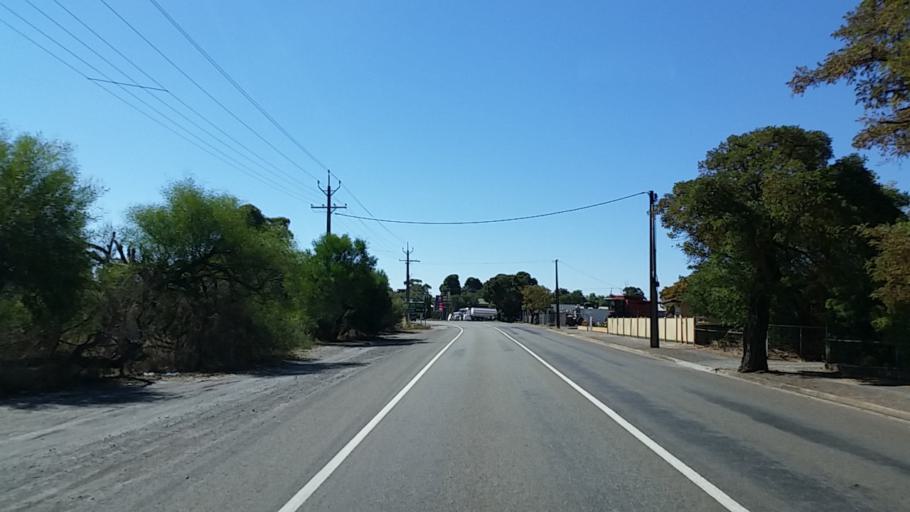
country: AU
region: South Australia
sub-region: Light
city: Kapunda
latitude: -34.0845
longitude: 138.7792
